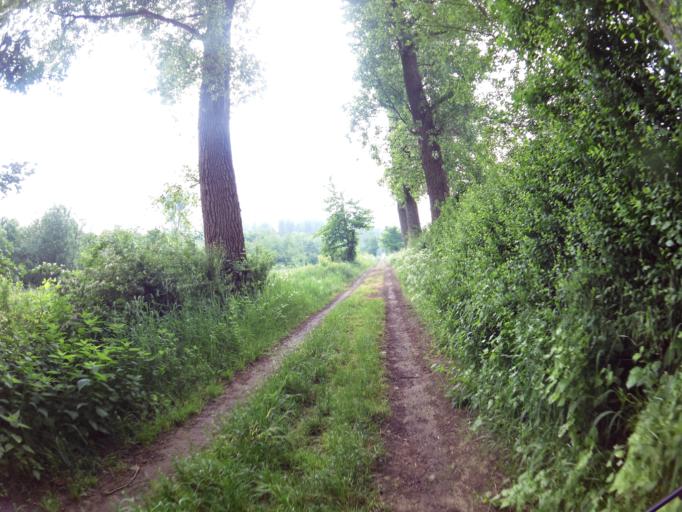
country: DE
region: North Rhine-Westphalia
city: Huckelhoven
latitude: 51.0117
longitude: 6.1802
